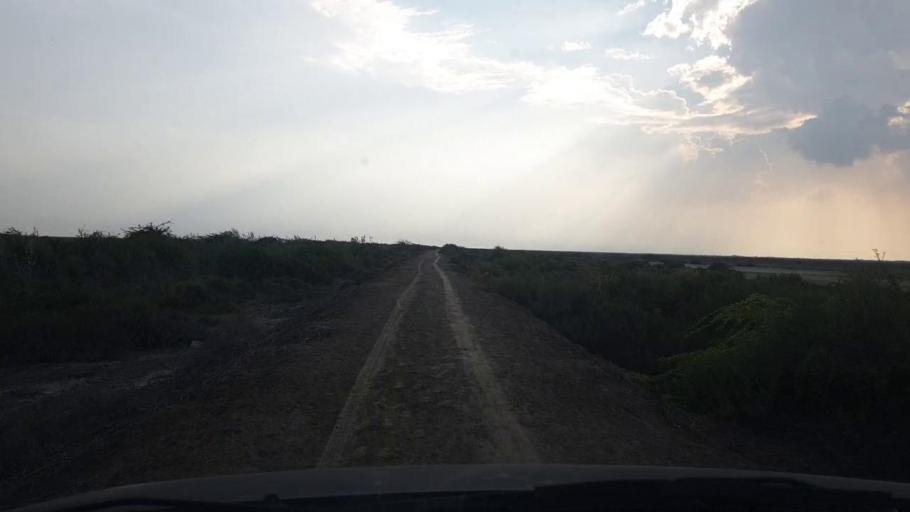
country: PK
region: Sindh
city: Badin
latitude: 24.4613
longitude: 68.6902
